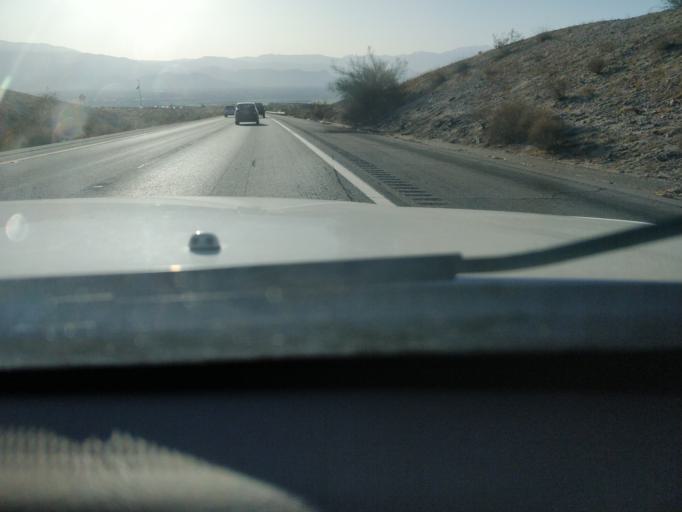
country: US
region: California
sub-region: Riverside County
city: Thermal
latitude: 33.7005
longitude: -116.0856
